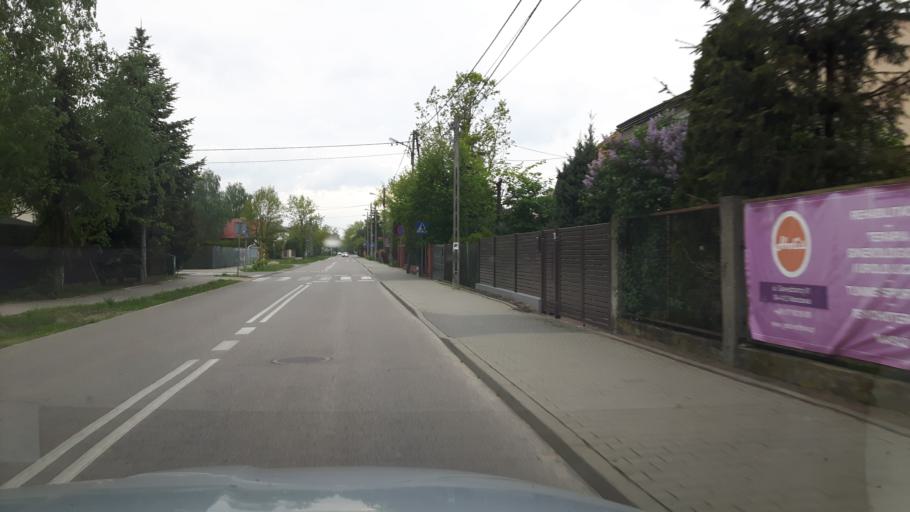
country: PL
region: Masovian Voivodeship
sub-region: Warszawa
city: Rembertow
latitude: 52.2689
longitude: 21.1631
